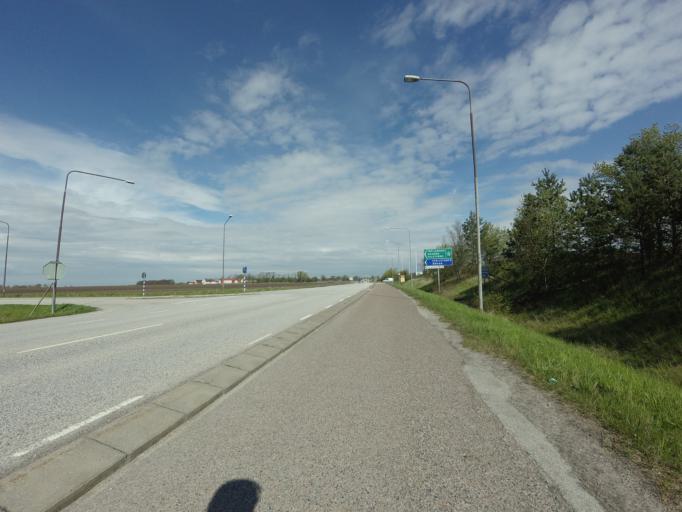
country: SE
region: Skane
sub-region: Vellinge Kommun
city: Vellinge
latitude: 55.4814
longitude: 13.0150
